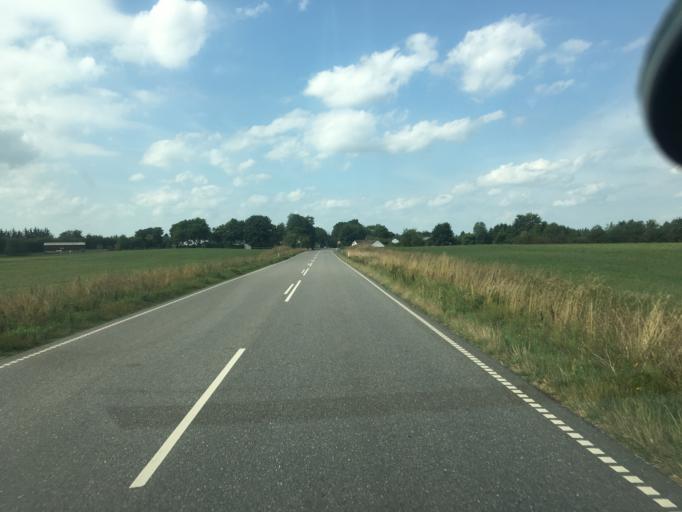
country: DK
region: South Denmark
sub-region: Aabenraa Kommune
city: Tinglev
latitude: 54.9366
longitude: 9.3329
